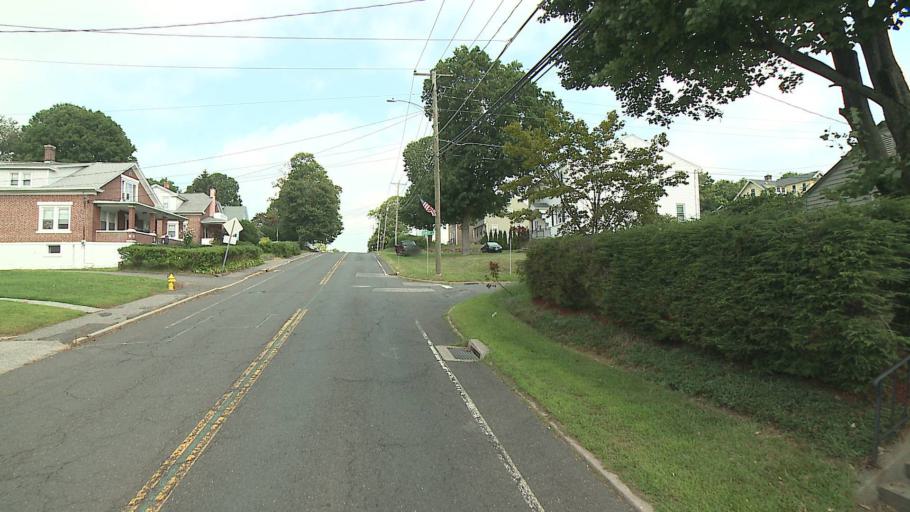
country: US
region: Connecticut
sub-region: Litchfield County
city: Oakville
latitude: 41.5946
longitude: -73.0834
